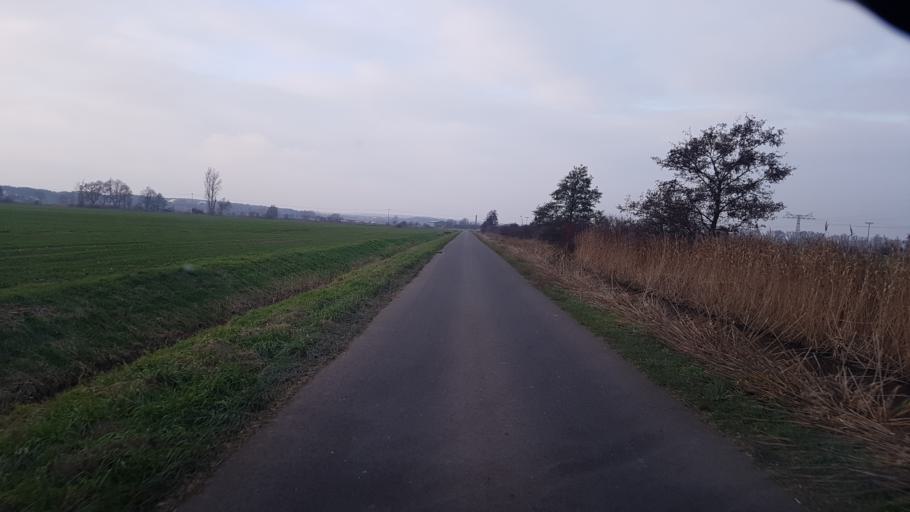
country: DE
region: Brandenburg
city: Wiesenau
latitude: 52.2311
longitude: 14.6107
